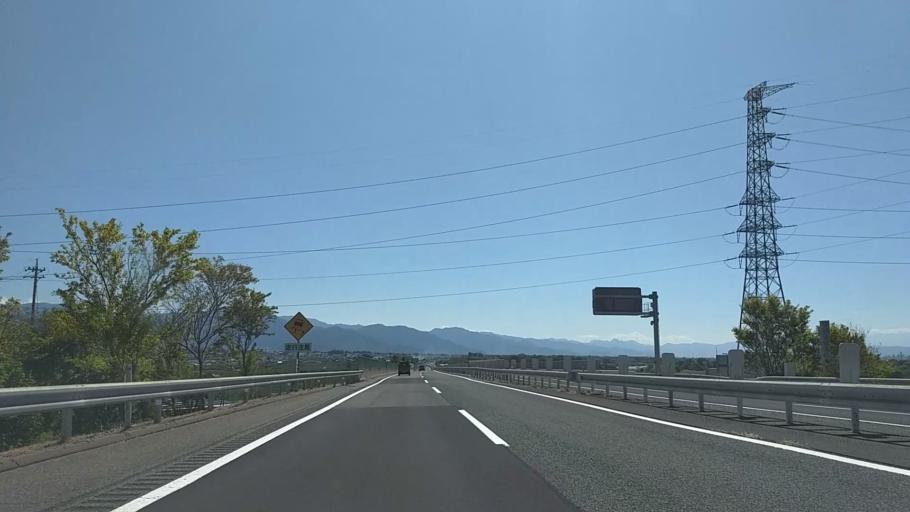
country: JP
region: Nagano
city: Nakano
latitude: 36.7255
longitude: 138.3165
